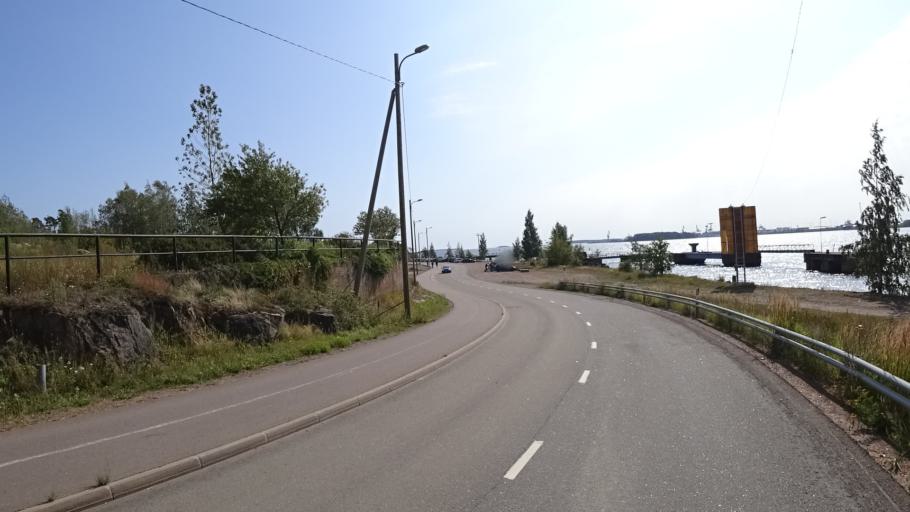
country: FI
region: Kymenlaakso
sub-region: Kotka-Hamina
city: Kotka
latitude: 60.4506
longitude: 26.9338
